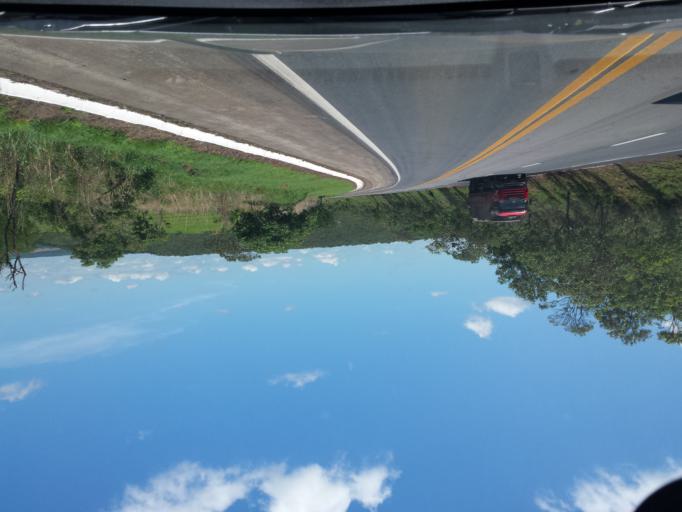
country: BR
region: Goias
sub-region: Luziania
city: Luziania
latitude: -16.3704
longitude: -47.8273
